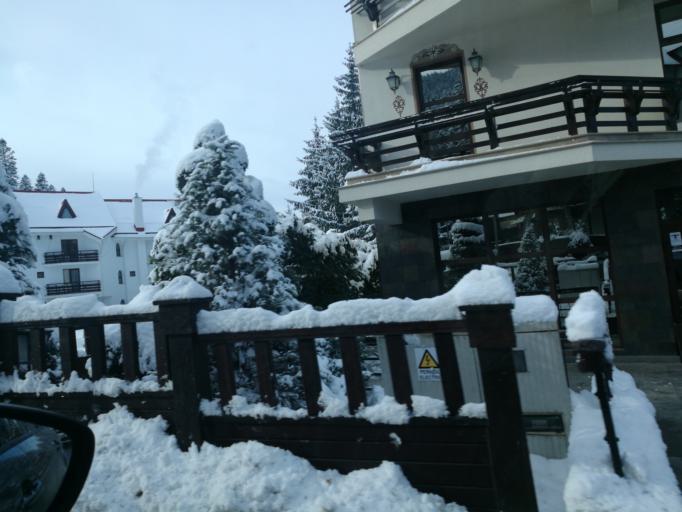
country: RO
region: Brasov
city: Brasov
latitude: 45.5885
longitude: 25.5513
